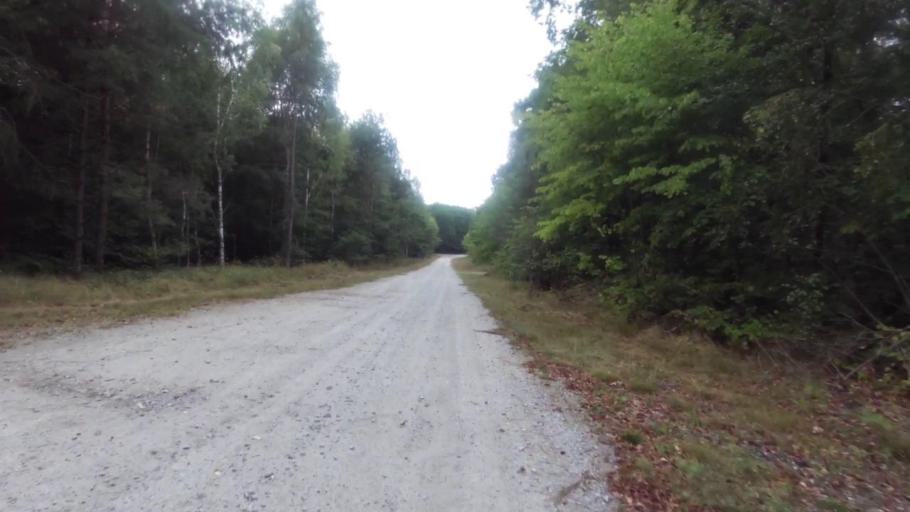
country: PL
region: Lubusz
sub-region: Powiat gorzowski
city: Kostrzyn nad Odra
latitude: 52.6222
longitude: 14.6510
